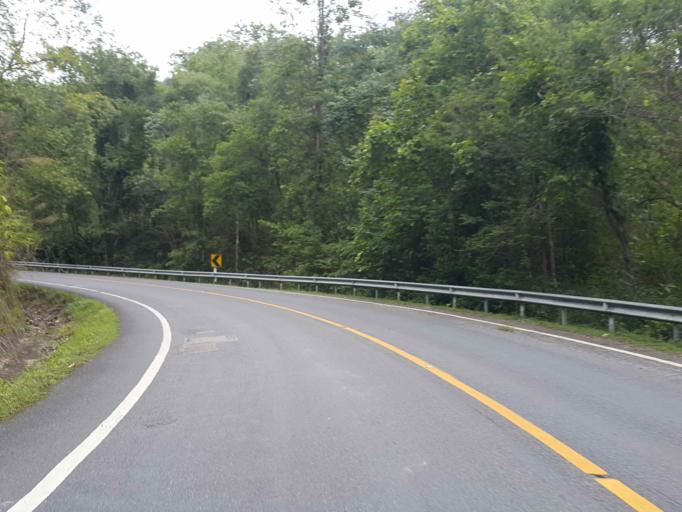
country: TH
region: Chiang Mai
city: Chom Thong
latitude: 18.5291
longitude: 98.6253
